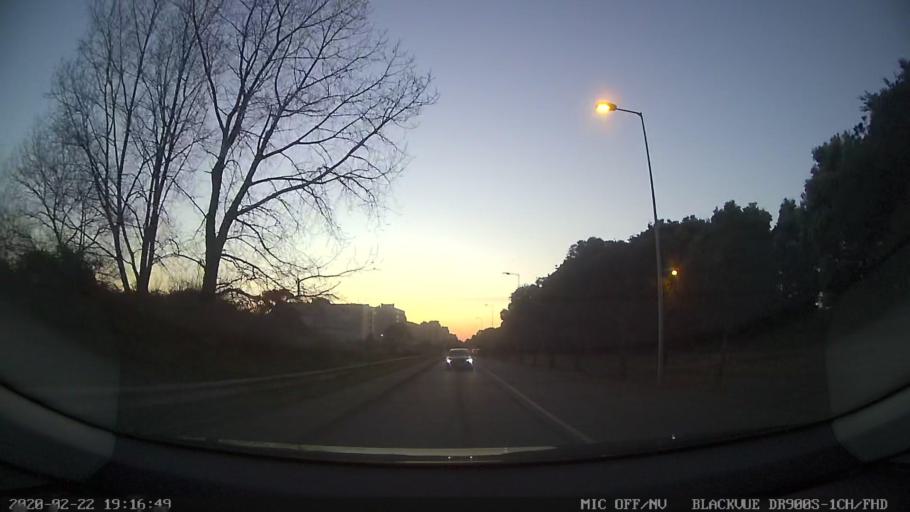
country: PT
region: Porto
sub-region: Matosinhos
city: Leca da Palmeira
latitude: 41.2013
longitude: -8.7010
